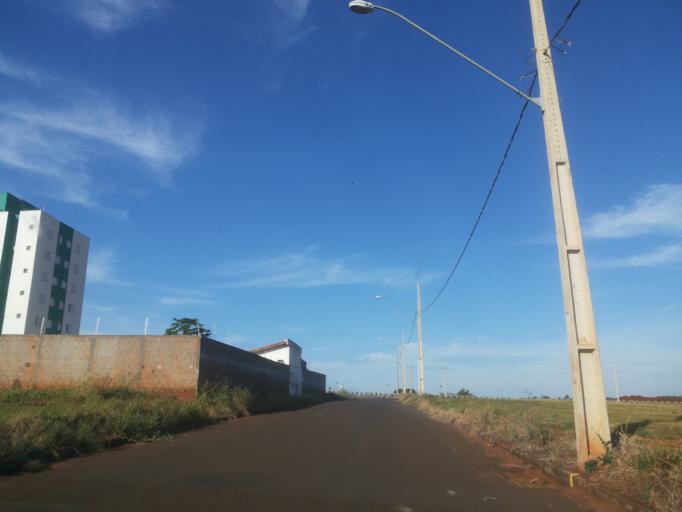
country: BR
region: Minas Gerais
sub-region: Ituiutaba
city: Ituiutaba
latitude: -18.9988
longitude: -49.4683
